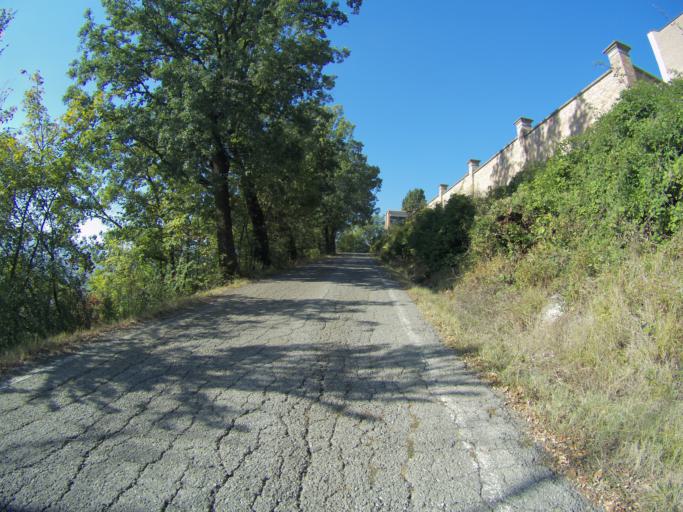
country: IT
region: Emilia-Romagna
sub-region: Provincia di Reggio Emilia
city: Puianello
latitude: 44.6213
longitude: 10.5544
